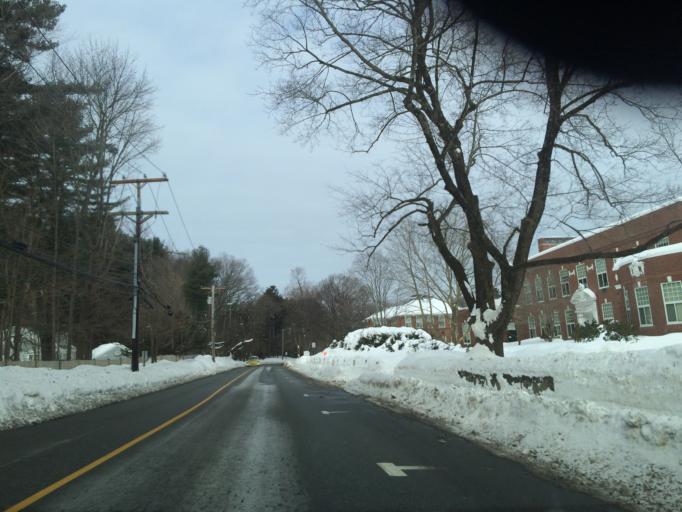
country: US
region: Massachusetts
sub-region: Middlesex County
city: Weston
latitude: 42.3645
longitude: -71.2945
